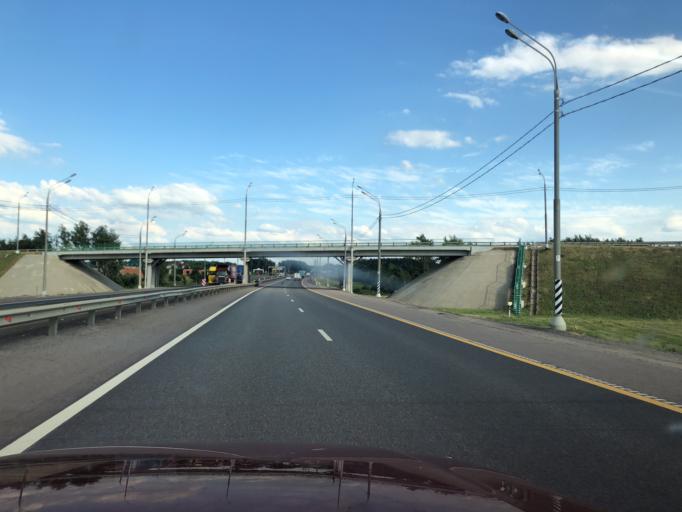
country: RU
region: Lipetsk
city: Zadonsk
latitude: 52.4365
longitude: 38.8148
